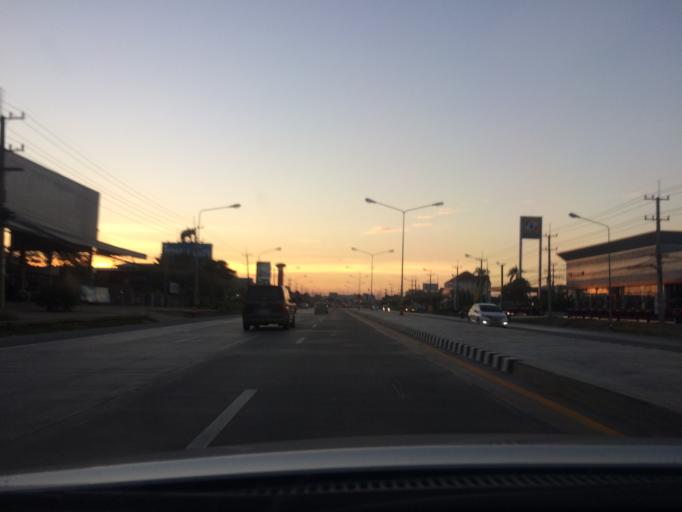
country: TH
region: Phitsanulok
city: Phitsanulok
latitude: 16.8164
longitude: 100.3104
